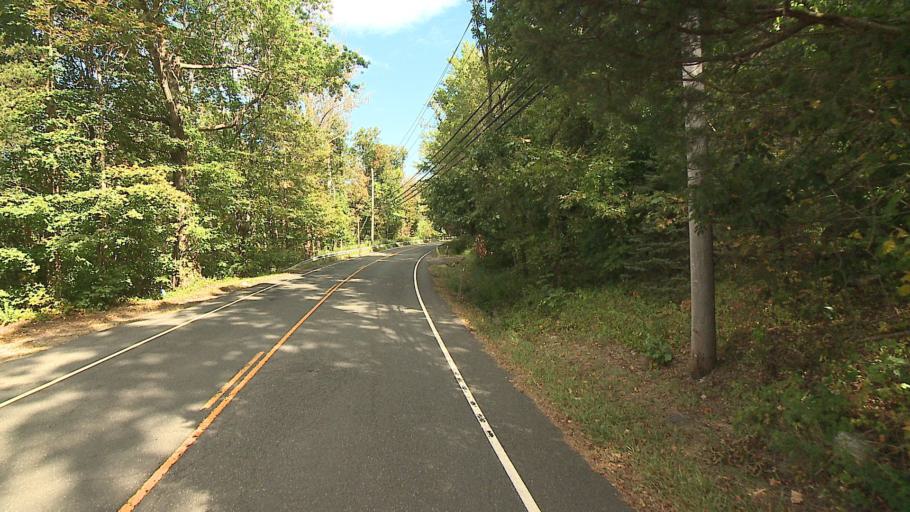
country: US
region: Connecticut
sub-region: Fairfield County
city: Wilton
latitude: 41.1722
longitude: -73.4469
